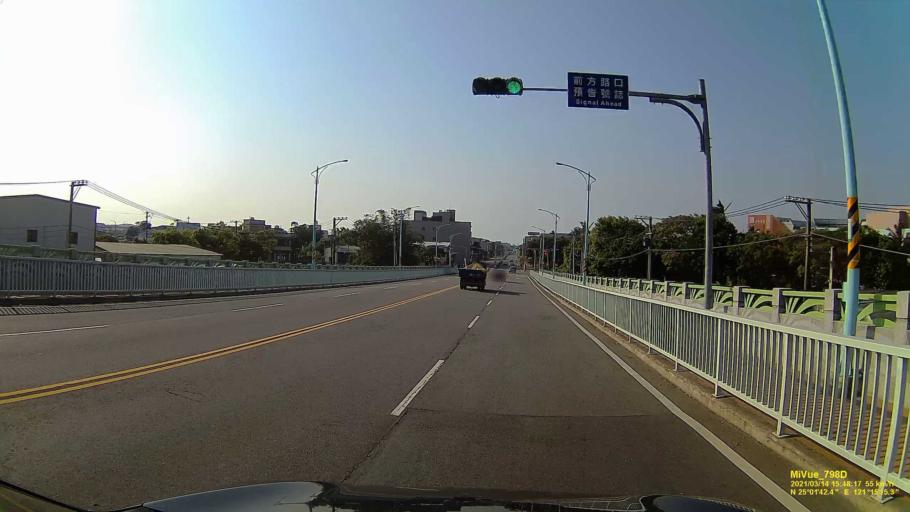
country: TW
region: Taiwan
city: Taoyuan City
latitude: 25.0284
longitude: 121.2543
